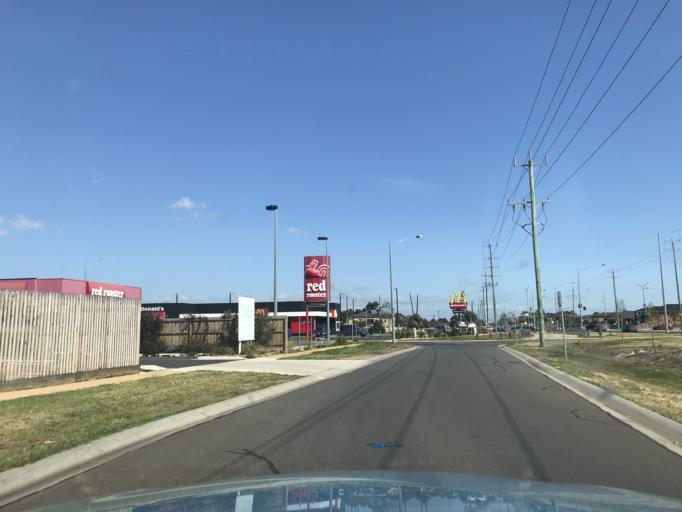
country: AU
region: Victoria
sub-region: Wyndham
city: Williams Landing
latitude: -37.8531
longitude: 144.7331
